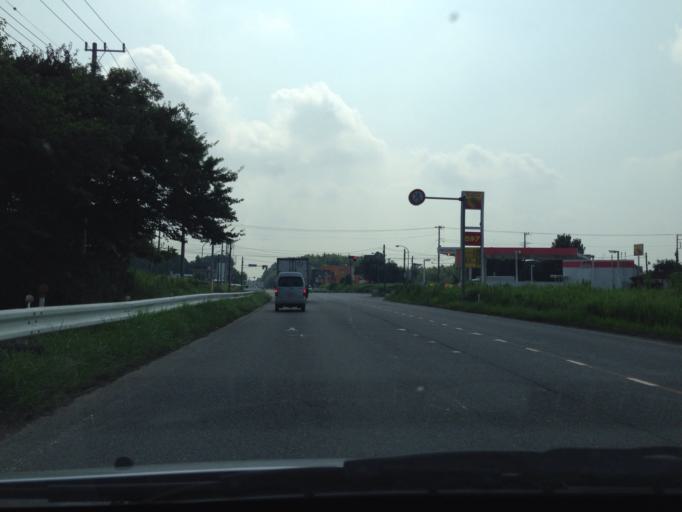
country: JP
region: Ibaraki
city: Ami
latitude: 36.0219
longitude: 140.2428
